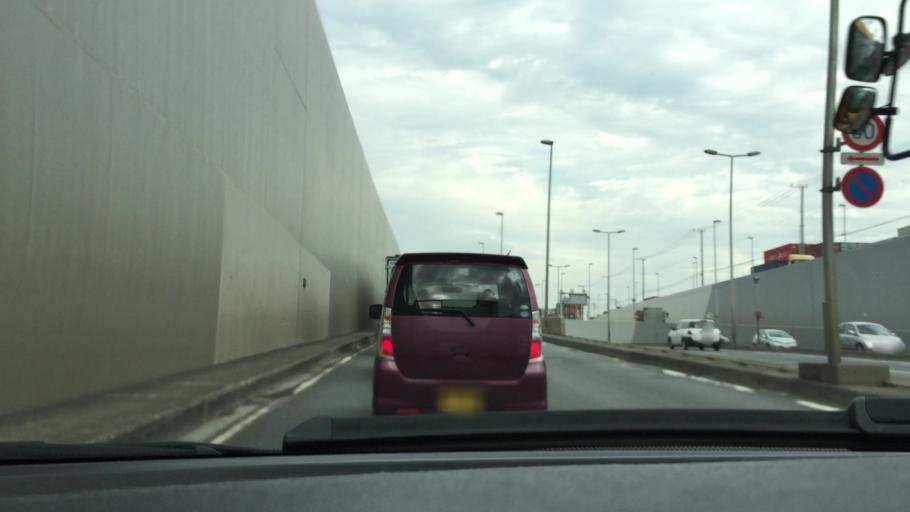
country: JP
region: Kanagawa
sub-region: Kawasaki-shi
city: Kawasaki
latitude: 35.5933
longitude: 139.7960
